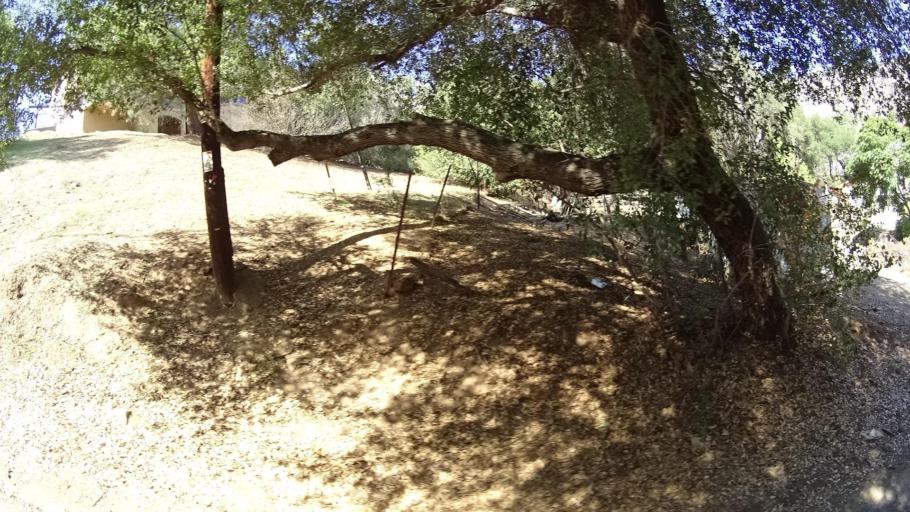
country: US
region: California
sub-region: San Diego County
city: Harbison Canyon
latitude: 32.8204
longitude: -116.8312
